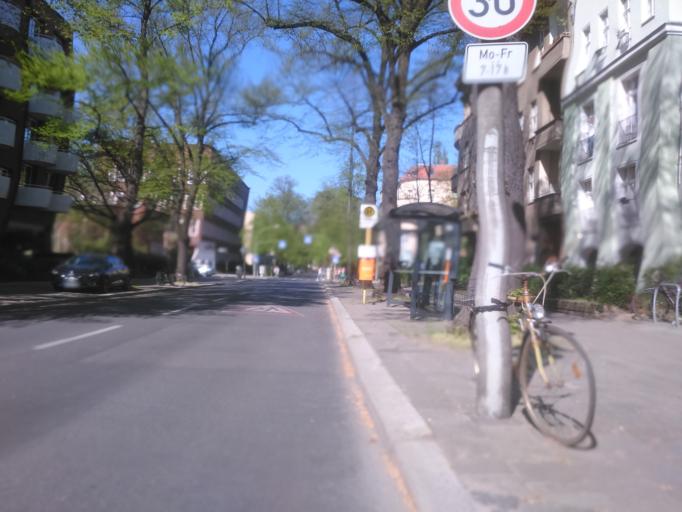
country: DE
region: Berlin
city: Weissensee
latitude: 52.5543
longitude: 13.4578
